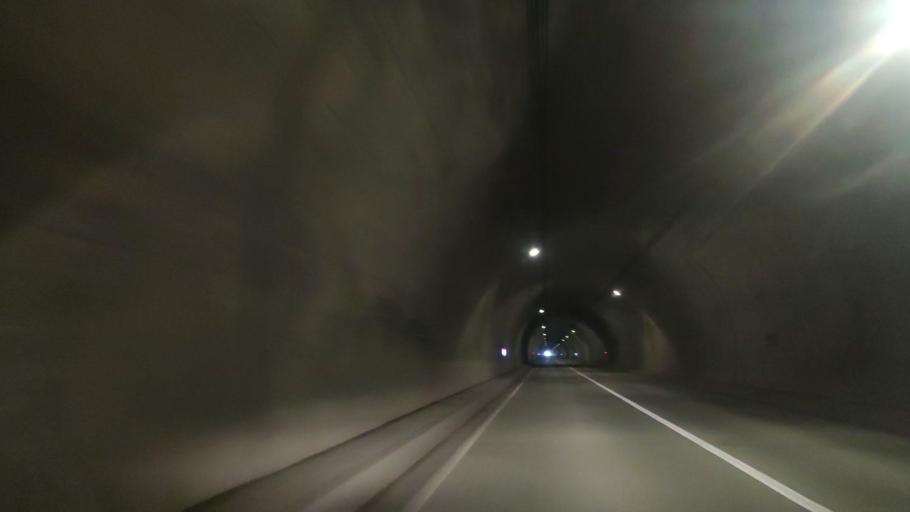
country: JP
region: Hokkaido
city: Iwamizawa
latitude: 43.0335
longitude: 142.0909
